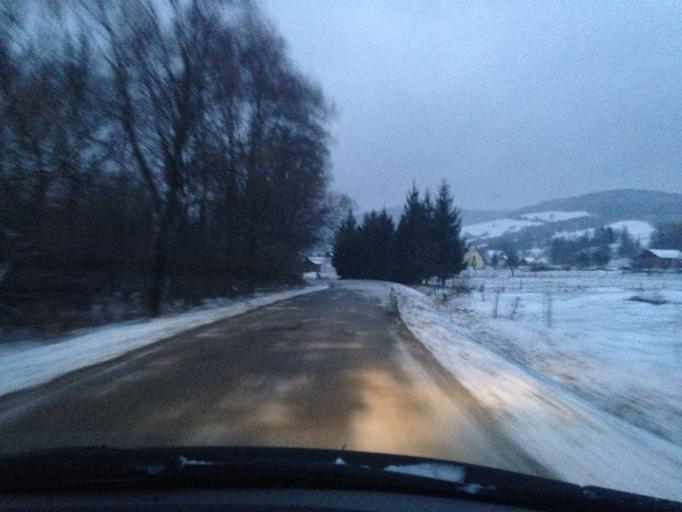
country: PL
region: Subcarpathian Voivodeship
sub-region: Powiat jasielski
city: Krempna
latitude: 49.5328
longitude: 21.5512
